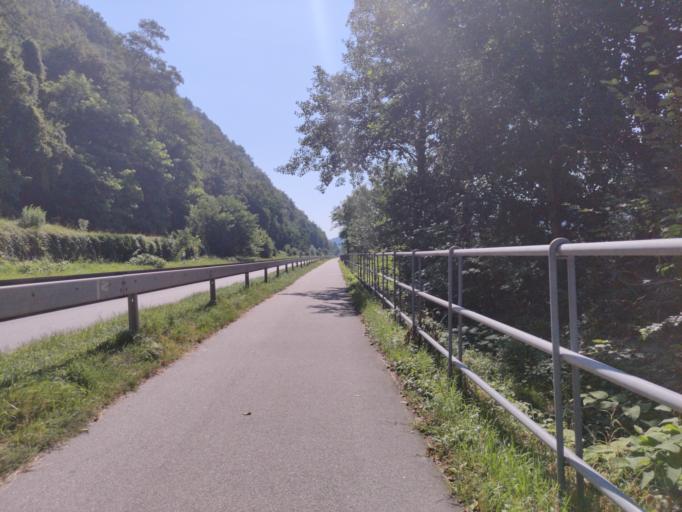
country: DE
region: Bavaria
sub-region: Lower Bavaria
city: Obernzell
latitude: 48.5657
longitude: 13.6090
